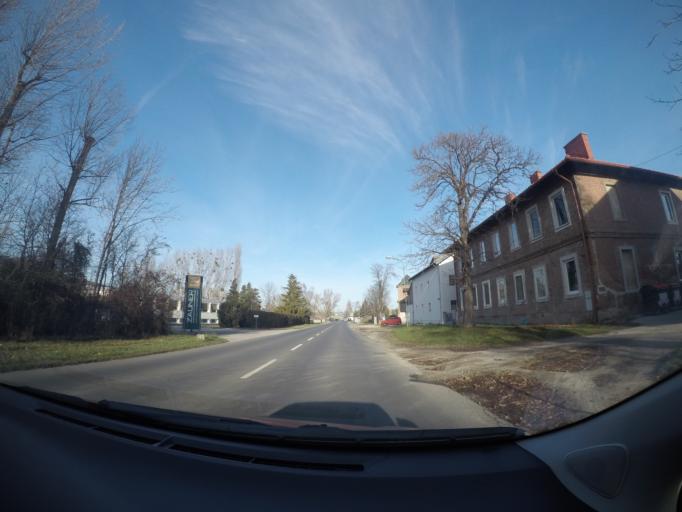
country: AT
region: Lower Austria
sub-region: Politischer Bezirk Baden
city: Traiskirchen
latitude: 48.0262
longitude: 16.2853
